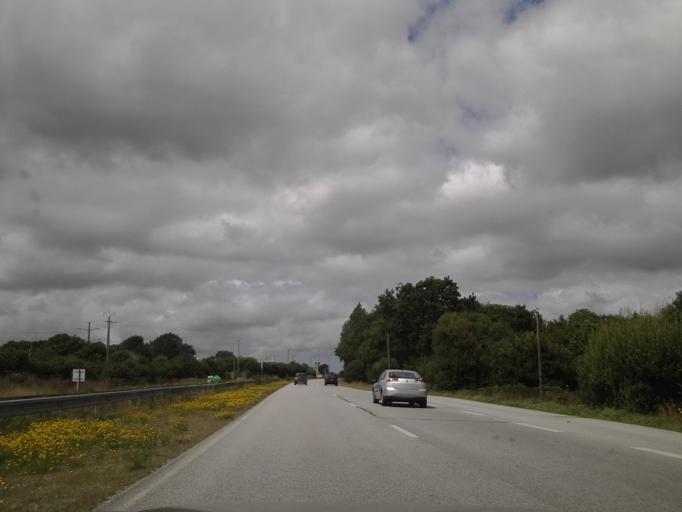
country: FR
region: Lower Normandy
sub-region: Departement de la Manche
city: Brix
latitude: 49.5682
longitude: -1.5729
